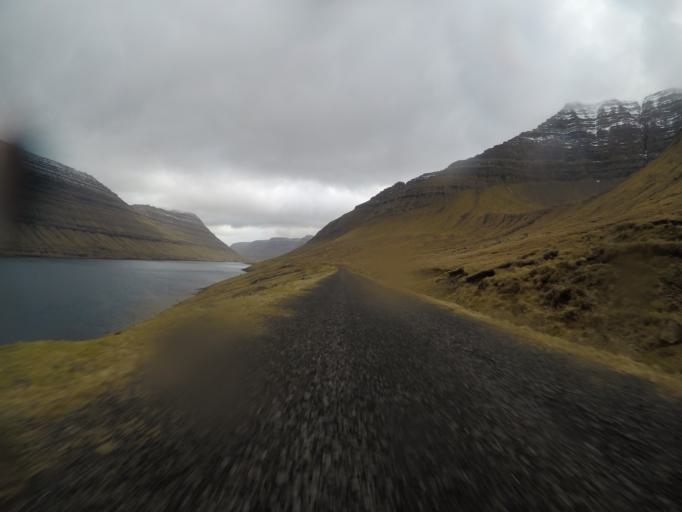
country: FO
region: Nordoyar
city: Klaksvik
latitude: 62.3206
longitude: -6.5594
